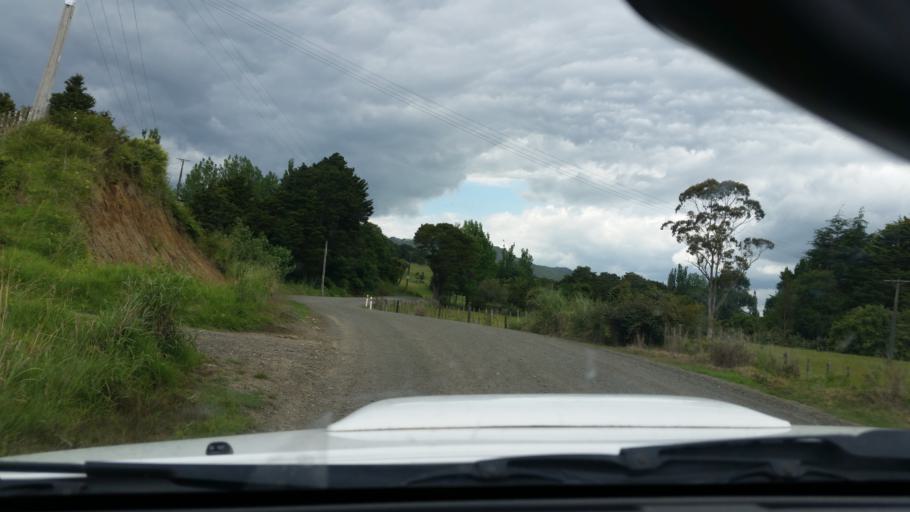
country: NZ
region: Northland
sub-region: Kaipara District
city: Dargaville
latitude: -35.8135
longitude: 173.8934
